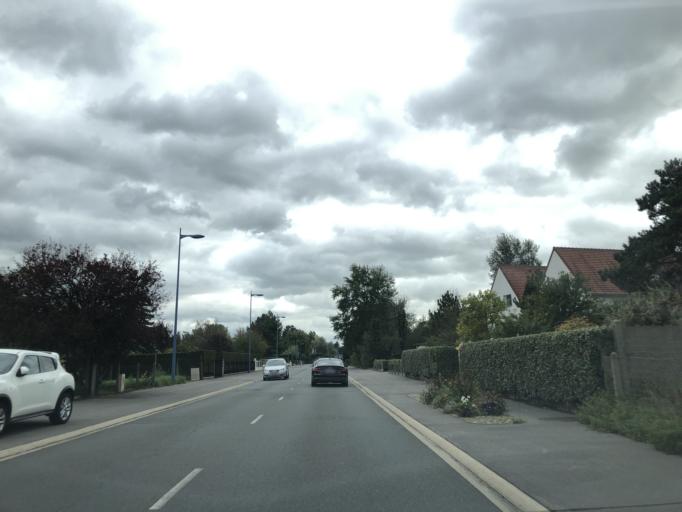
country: FR
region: Nord-Pas-de-Calais
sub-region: Departement du Pas-de-Calais
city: Cucq
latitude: 50.4706
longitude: 1.6166
